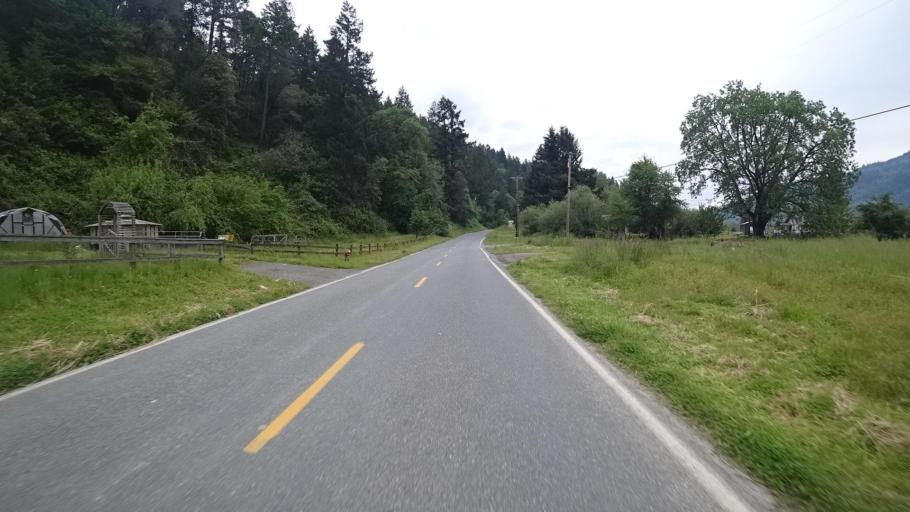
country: US
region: California
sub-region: Humboldt County
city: Willow Creek
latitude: 41.0616
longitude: -123.6937
